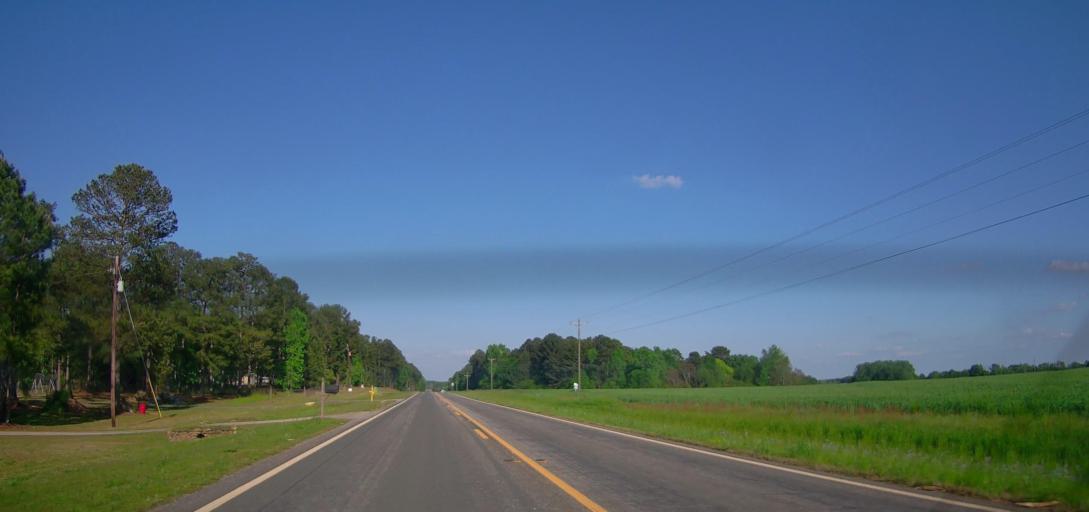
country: US
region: Georgia
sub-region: Walton County
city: Social Circle
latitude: 33.6242
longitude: -83.6341
